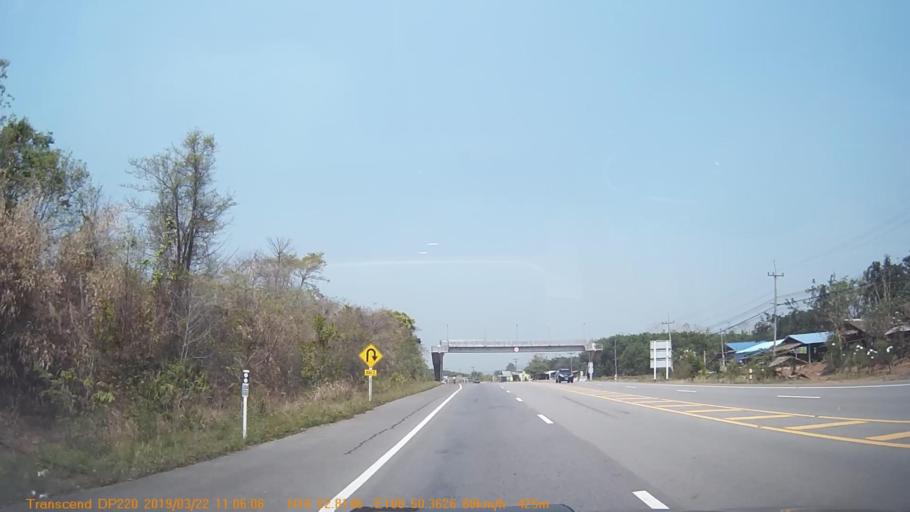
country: TH
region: Phitsanulok
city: Nakhon Thai
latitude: 16.8803
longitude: 100.8392
